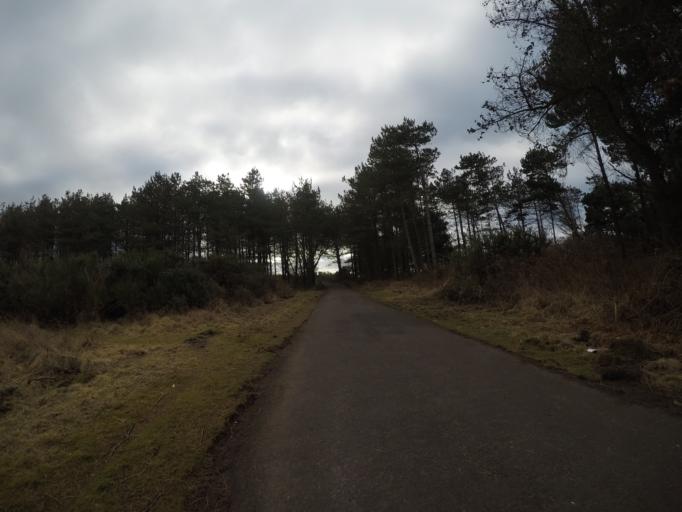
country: GB
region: Scotland
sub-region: North Ayrshire
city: Irvine
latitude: 55.5945
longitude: -4.6725
